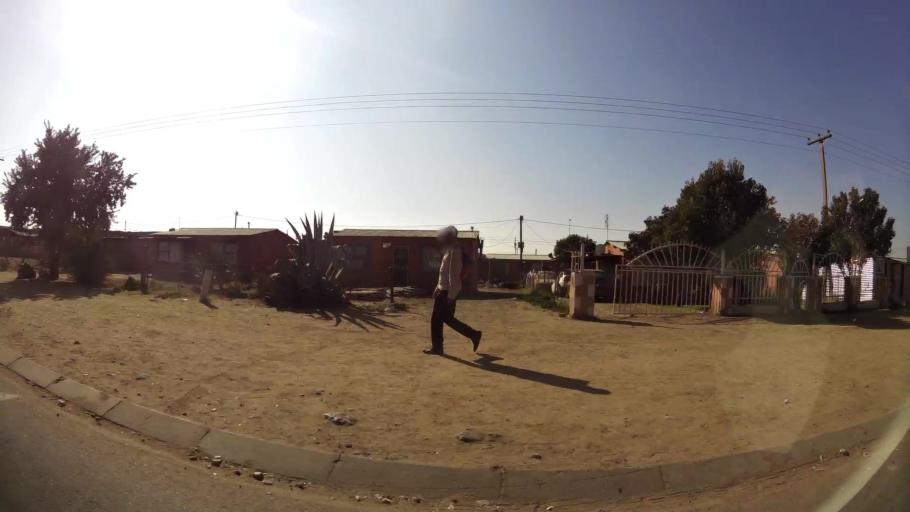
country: ZA
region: Orange Free State
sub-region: Mangaung Metropolitan Municipality
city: Bloemfontein
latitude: -29.1856
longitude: 26.2450
